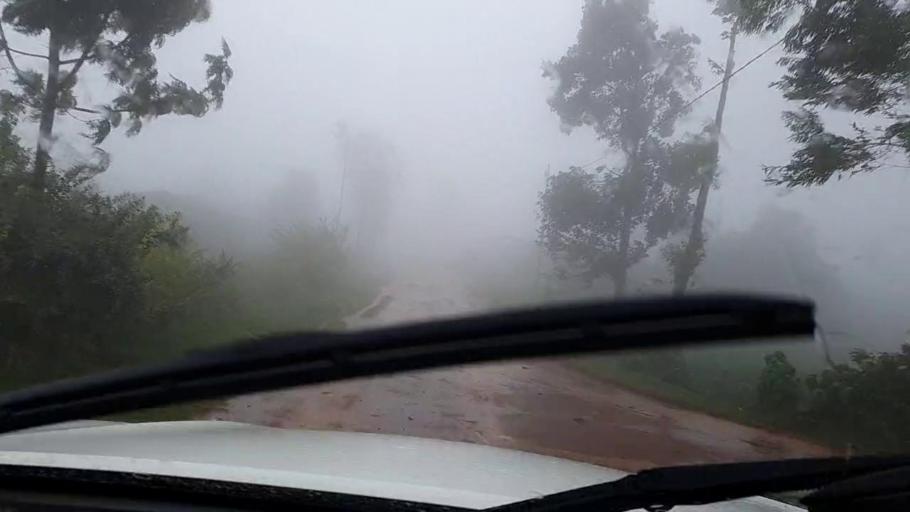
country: RW
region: Northern Province
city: Byumba
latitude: -1.7347
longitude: 30.0296
